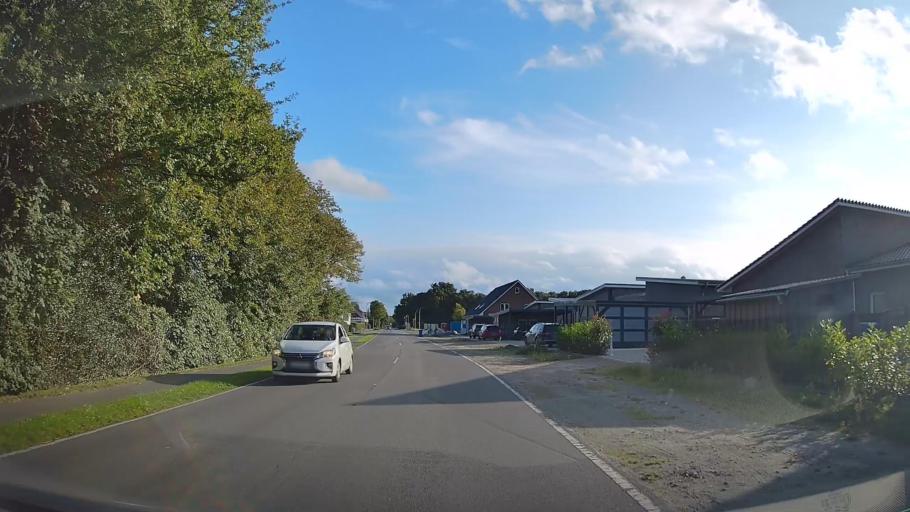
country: DE
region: Lower Saxony
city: Ostrhauderfehn
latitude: 53.1322
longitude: 7.6673
